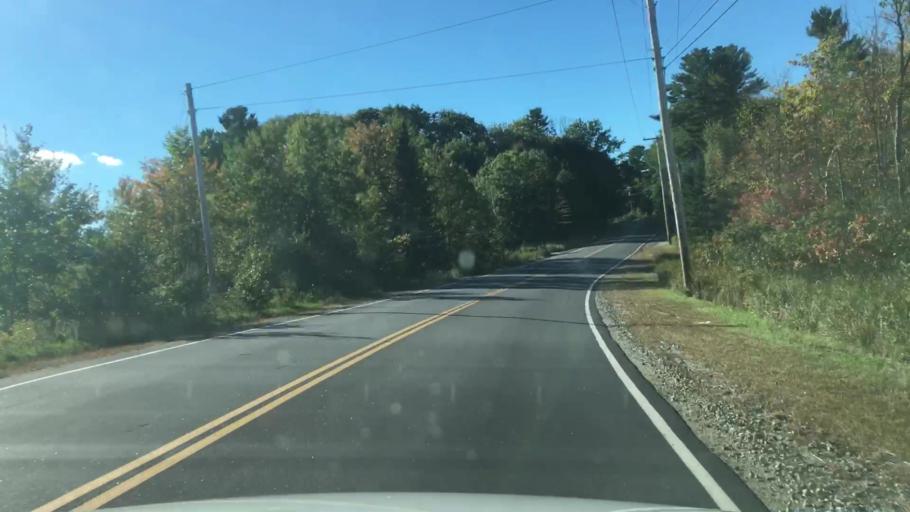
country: US
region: Maine
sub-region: Androscoggin County
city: Lisbon
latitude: 44.0737
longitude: -70.0980
